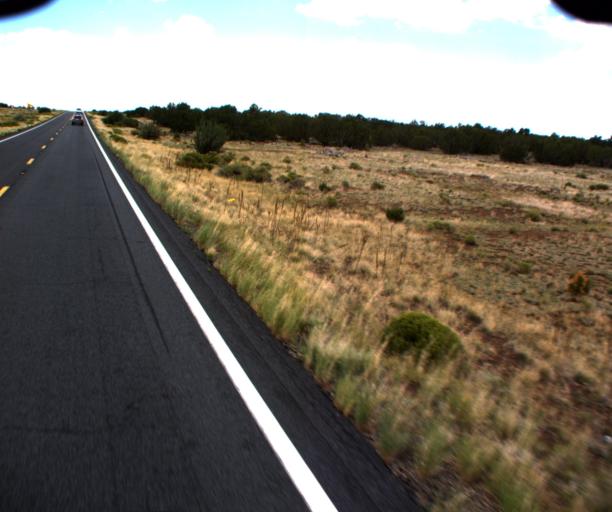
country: US
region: Arizona
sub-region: Coconino County
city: Parks
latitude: 35.5729
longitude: -111.9281
